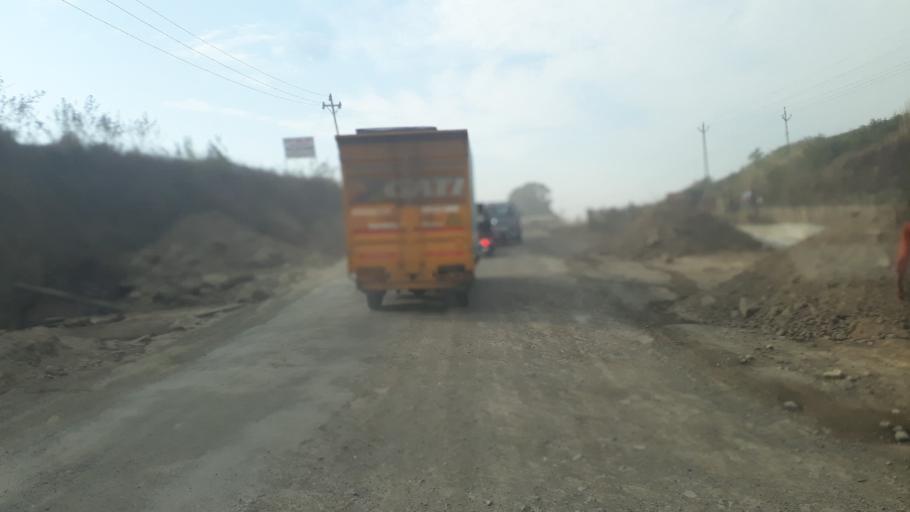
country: IN
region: Maharashtra
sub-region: Raigarh
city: Pen
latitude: 18.7709
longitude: 73.0921
